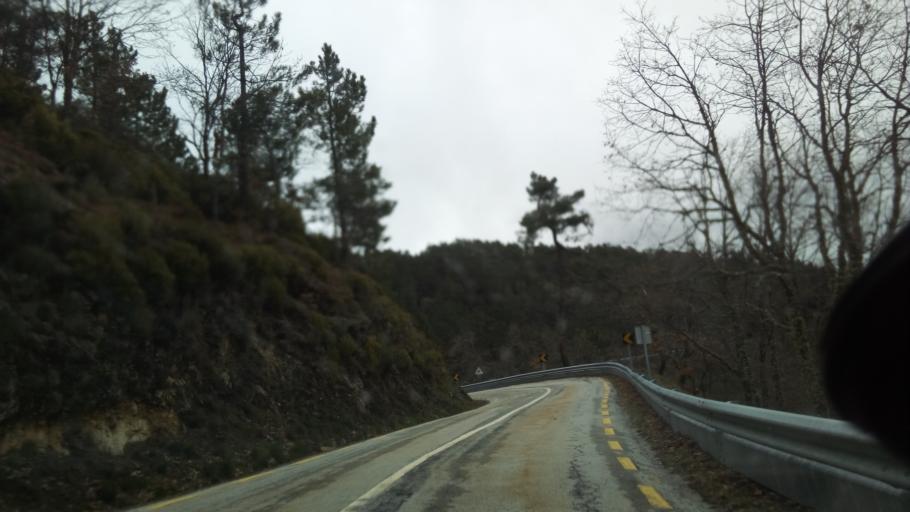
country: PT
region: Guarda
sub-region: Manteigas
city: Manteigas
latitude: 40.4133
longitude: -7.5515
